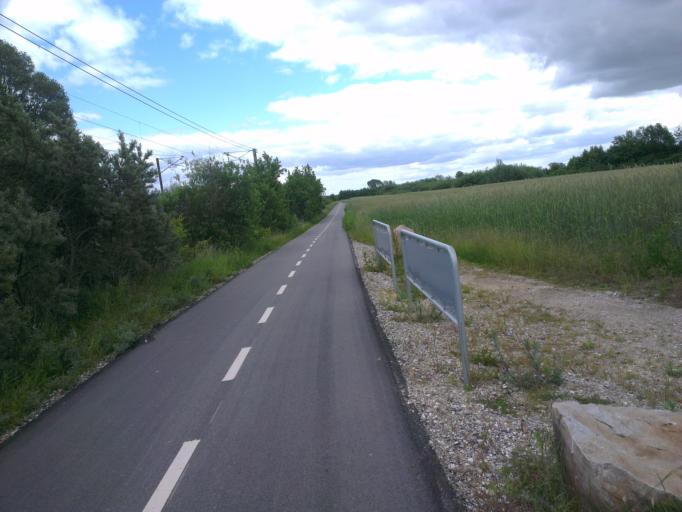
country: DK
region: Capital Region
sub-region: Frederikssund Kommune
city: Frederikssund
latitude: 55.8169
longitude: 12.0885
